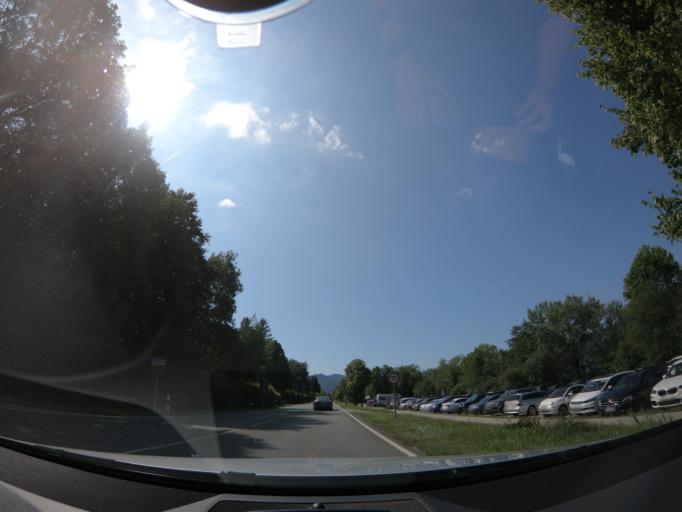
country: DE
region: Bavaria
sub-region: Upper Bavaria
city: Gmund am Tegernsee
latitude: 47.7414
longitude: 11.7376
